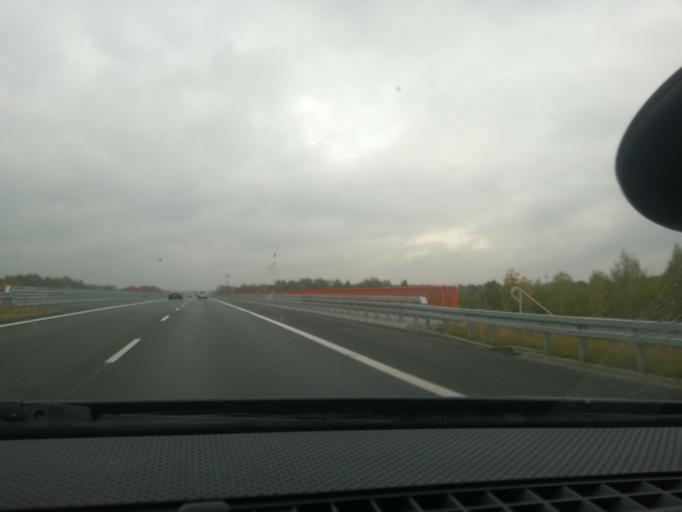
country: PL
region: Lodz Voivodeship
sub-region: Powiat lodzki wschodni
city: Andrespol
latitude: 51.7312
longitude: 19.6044
